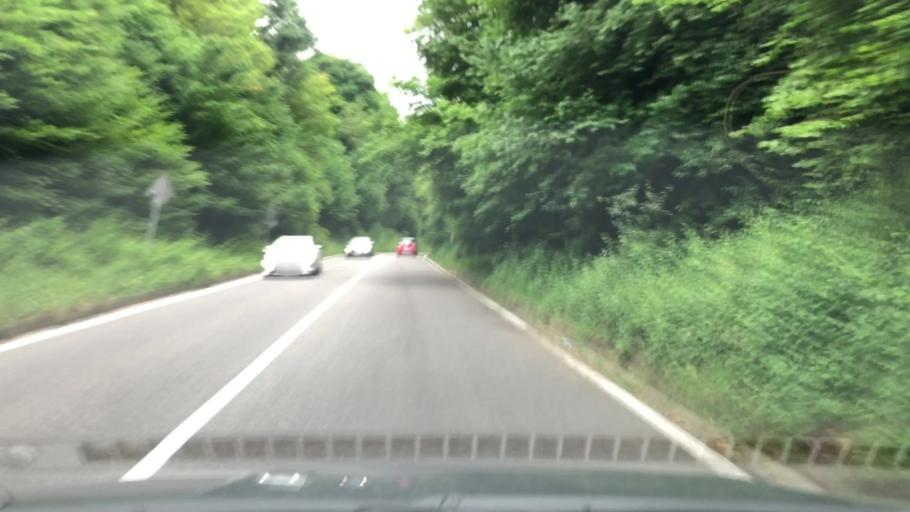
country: IT
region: Lombardy
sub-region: Provincia di Como
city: Fino Mornasco
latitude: 45.7404
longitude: 9.0663
